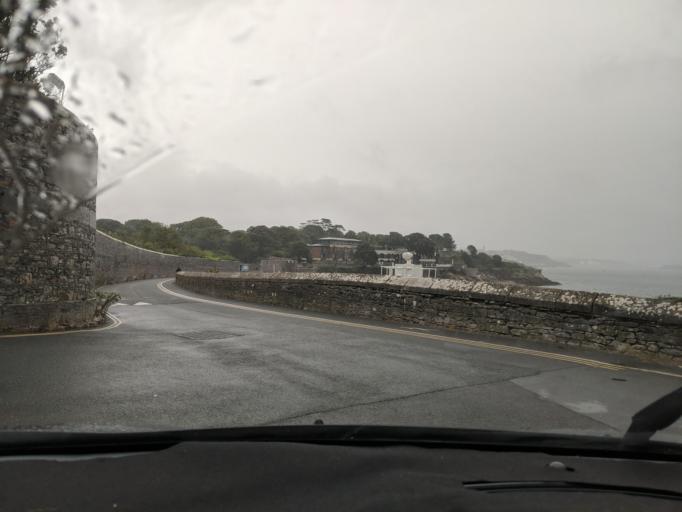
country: GB
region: England
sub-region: Cornwall
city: Millbrook
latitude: 50.3604
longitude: -4.1634
